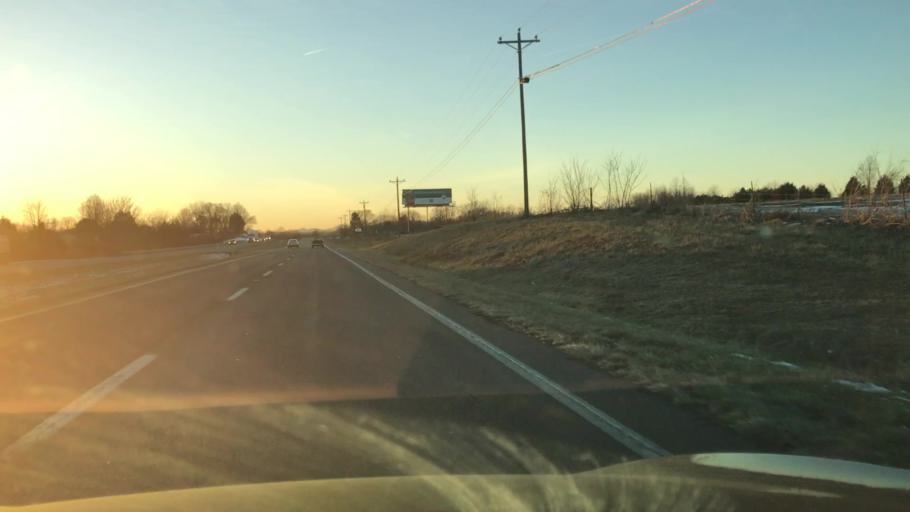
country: US
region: Virginia
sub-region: Bedford County
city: Forest
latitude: 37.3007
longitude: -79.3652
